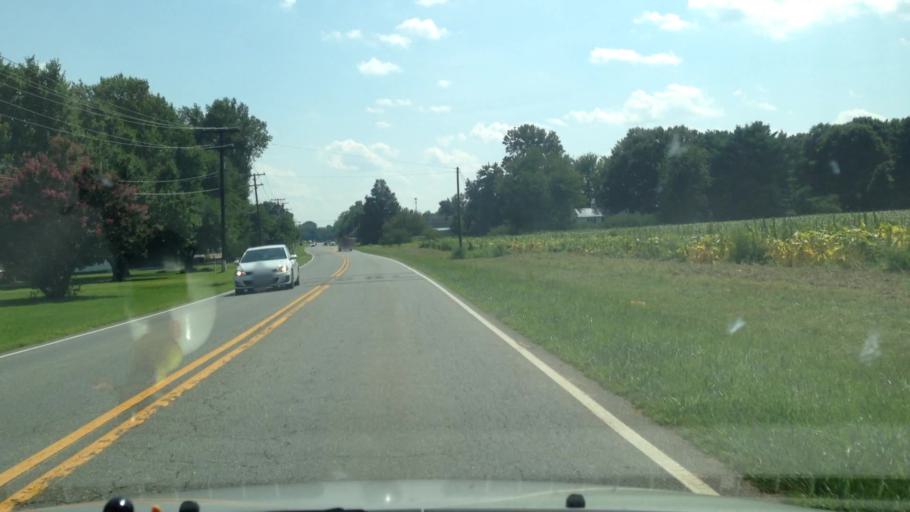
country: US
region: North Carolina
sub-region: Forsyth County
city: Kernersville
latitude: 36.1419
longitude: -80.0486
